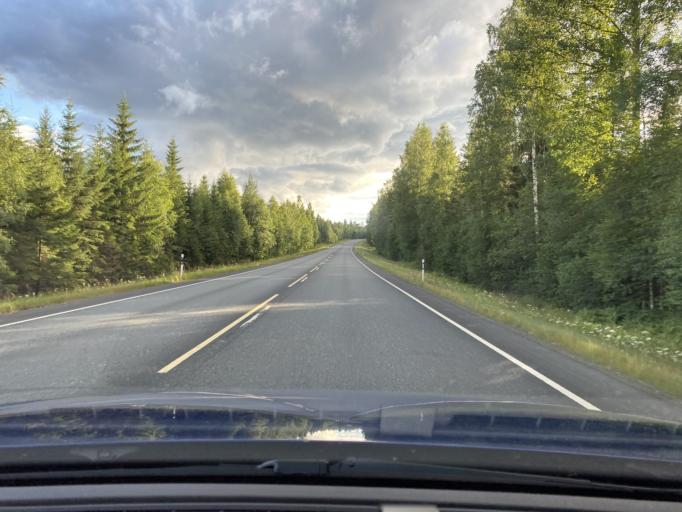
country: FI
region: Haeme
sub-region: Haemeenlinna
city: Renko
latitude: 60.8513
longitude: 24.1536
